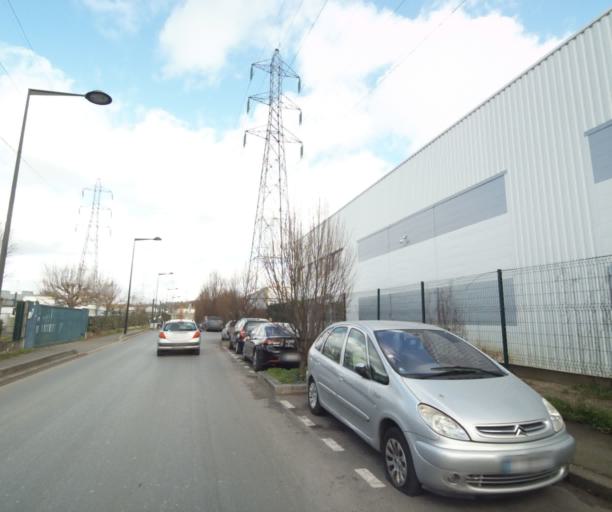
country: FR
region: Ile-de-France
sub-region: Departement de Seine-Saint-Denis
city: Villetaneuse
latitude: 48.9567
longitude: 2.3486
